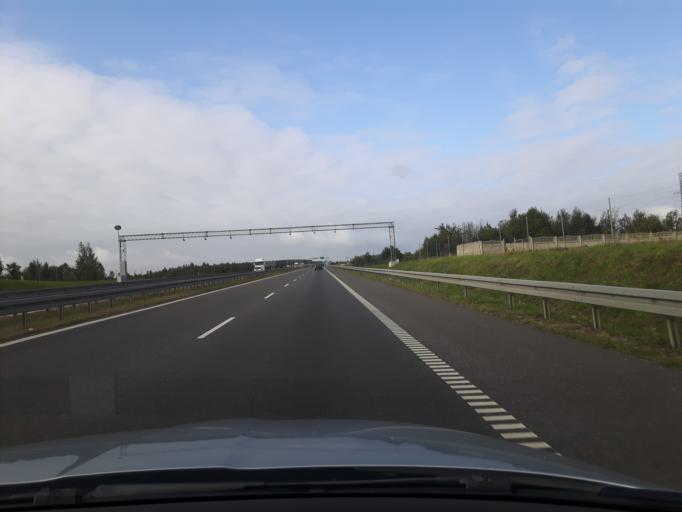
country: PL
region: Swietokrzyskie
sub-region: Powiat skarzyski
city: Laczna
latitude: 50.9975
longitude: 20.7856
